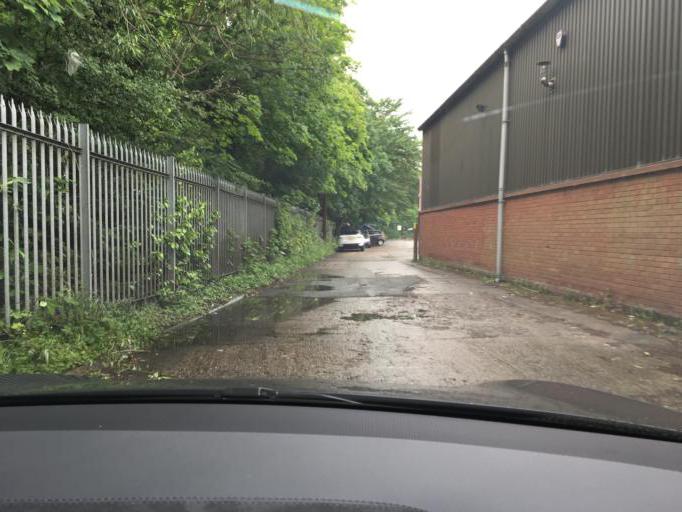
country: GB
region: England
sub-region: Borough of Stockport
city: Cheadle Heath
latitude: 53.3891
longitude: -2.2038
